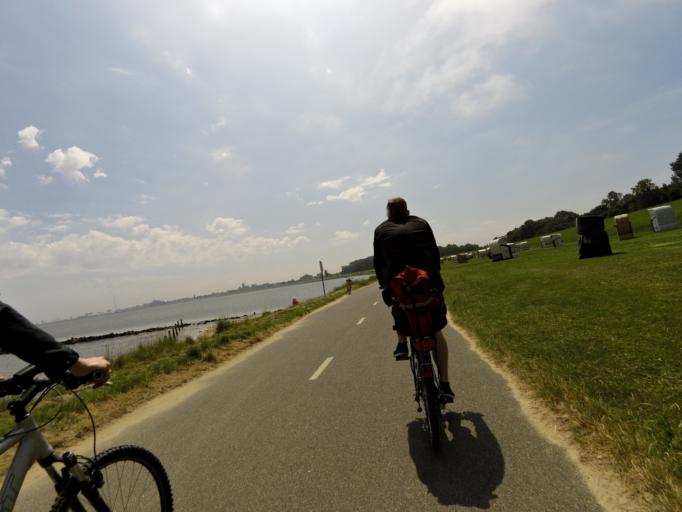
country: DE
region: Lower Saxony
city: Cuxhaven
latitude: 53.8895
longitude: 8.6836
